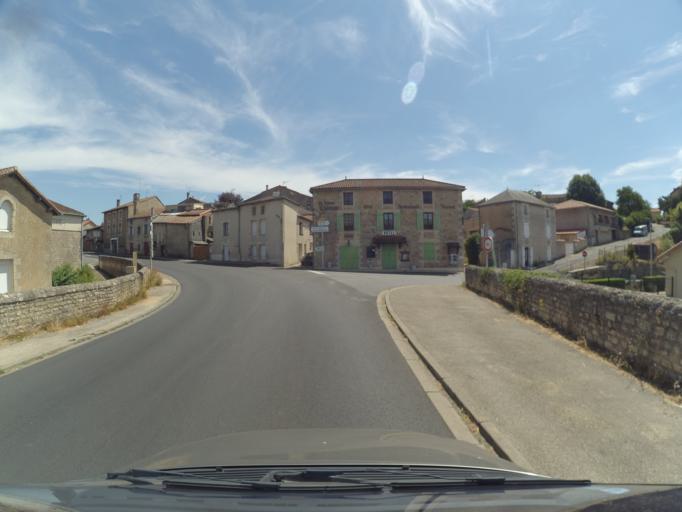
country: FR
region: Poitou-Charentes
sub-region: Departement de la Vienne
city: Saint-Maurice-la-Clouere
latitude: 46.3761
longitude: 0.4037
